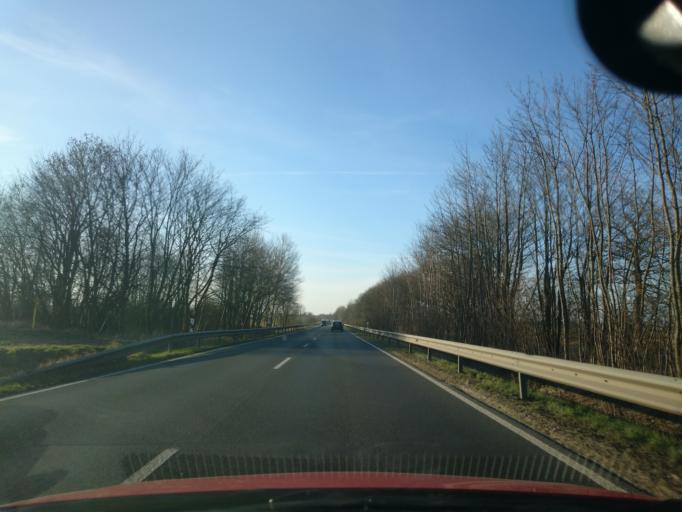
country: DE
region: Mecklenburg-Vorpommern
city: Mesekenhagen
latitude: 54.1370
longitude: 13.3375
